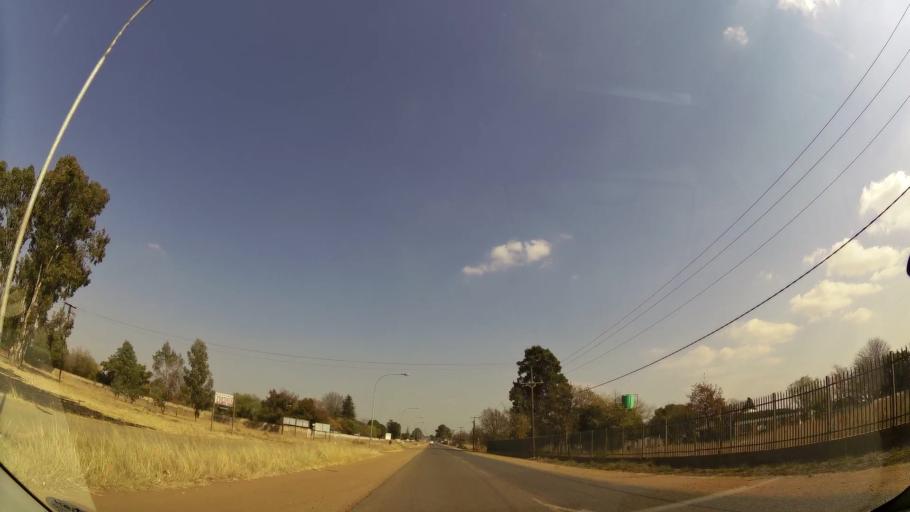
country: ZA
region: Gauteng
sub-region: Ekurhuleni Metropolitan Municipality
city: Benoni
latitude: -26.1184
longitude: 28.4043
